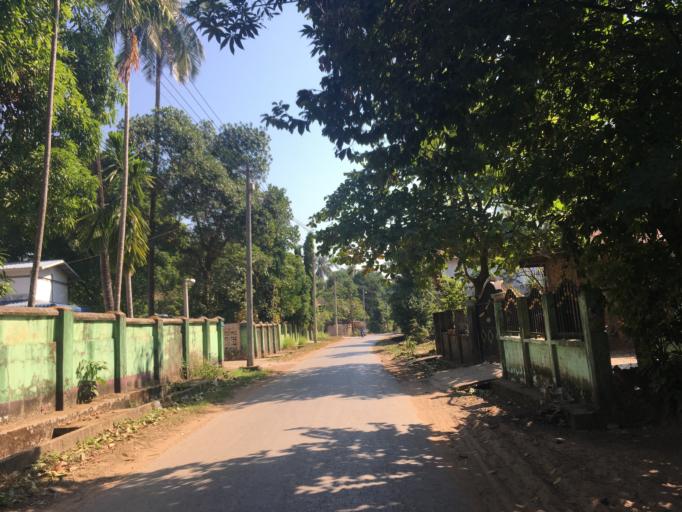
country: MM
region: Mon
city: Mawlamyine
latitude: 16.4322
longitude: 97.7021
